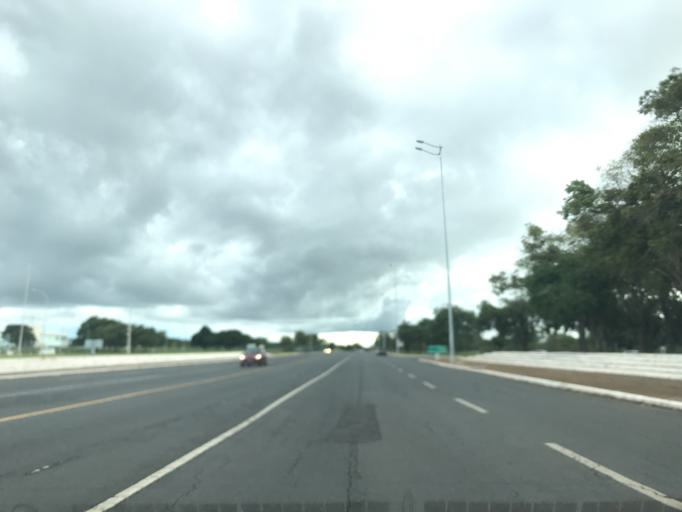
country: BR
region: Federal District
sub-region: Brasilia
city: Brasilia
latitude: -15.7743
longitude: -47.9205
